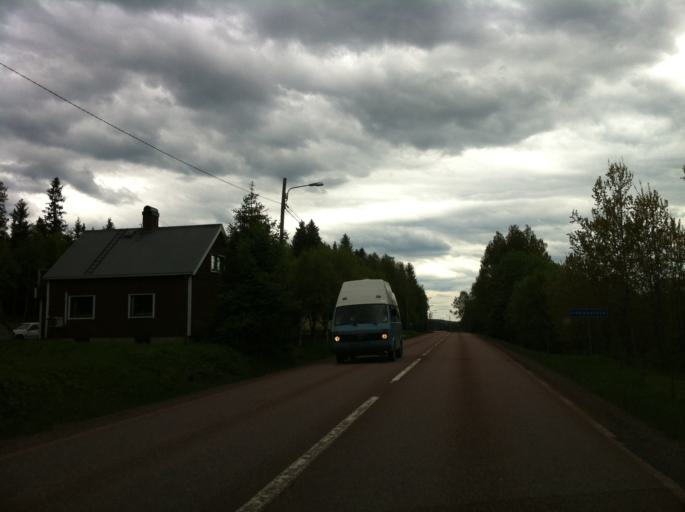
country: SE
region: Dalarna
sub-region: Malung-Saelens kommun
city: Malung
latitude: 61.0846
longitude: 13.3231
